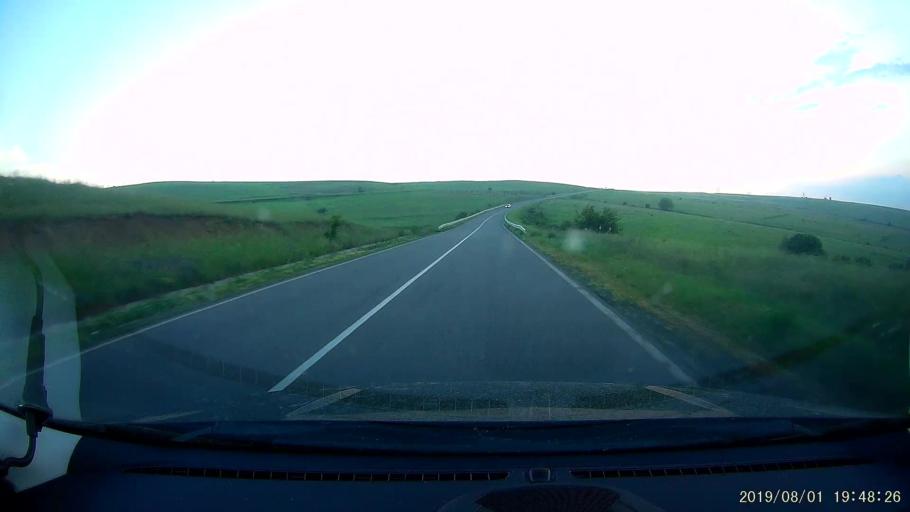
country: BG
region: Burgas
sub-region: Obshtina Karnobat
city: Karnobat
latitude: 42.6369
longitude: 26.9496
